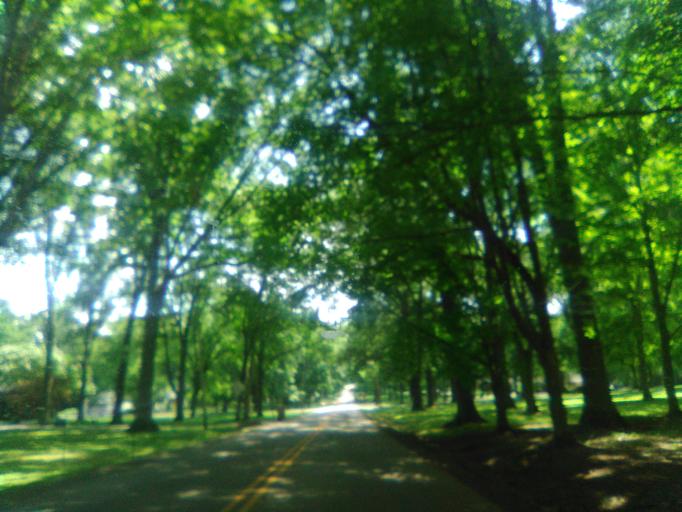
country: US
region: Tennessee
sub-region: Davidson County
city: Belle Meade
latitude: 36.1117
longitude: -86.8724
